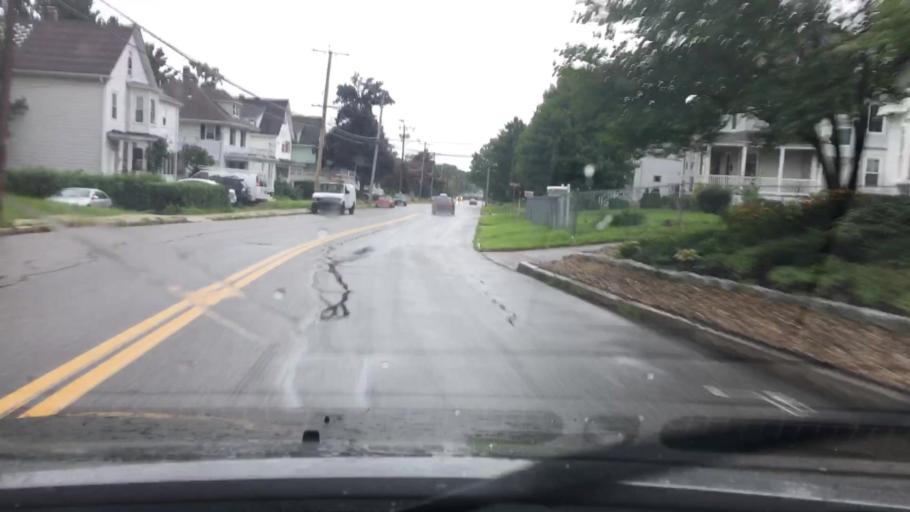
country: US
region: Massachusetts
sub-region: Worcester County
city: Milford
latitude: 42.1479
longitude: -71.5248
